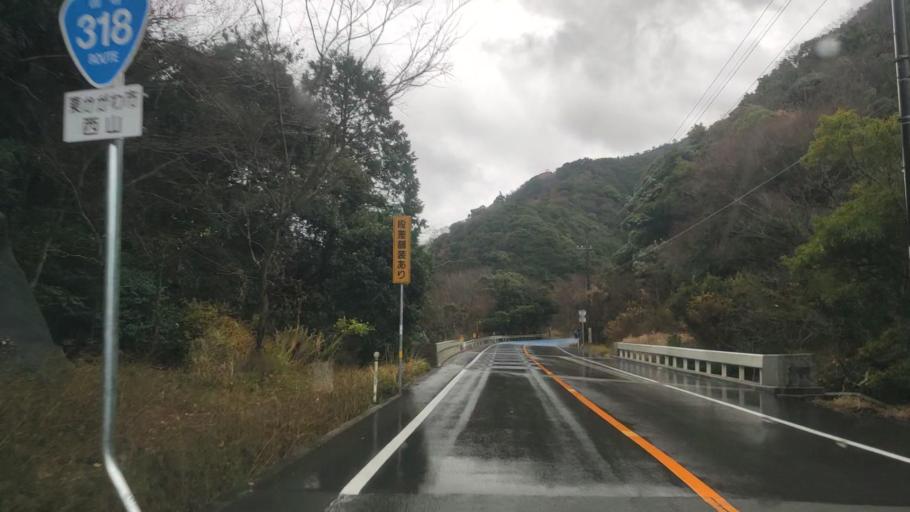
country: JP
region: Tokushima
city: Kamojimacho-jogejima
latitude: 34.1878
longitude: 134.3368
